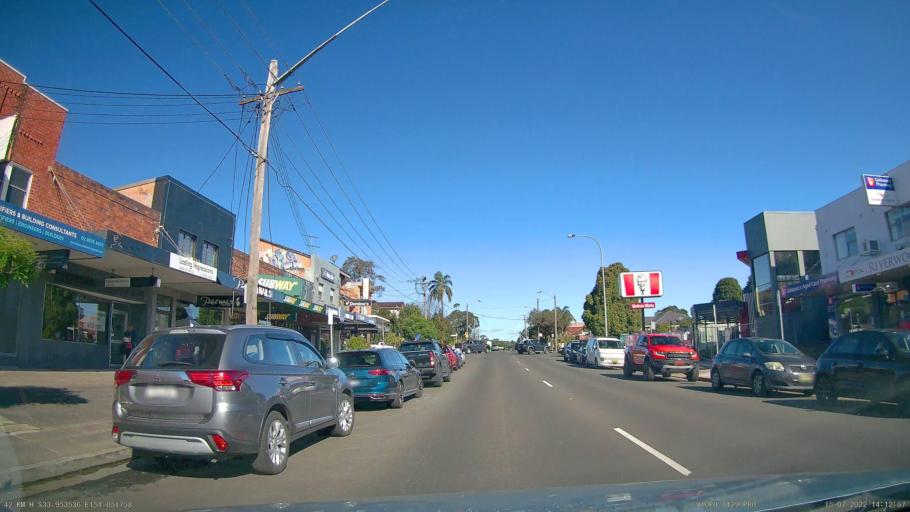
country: AU
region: New South Wales
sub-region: Hurstville
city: Peakhurst
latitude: -33.9537
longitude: 151.0517
